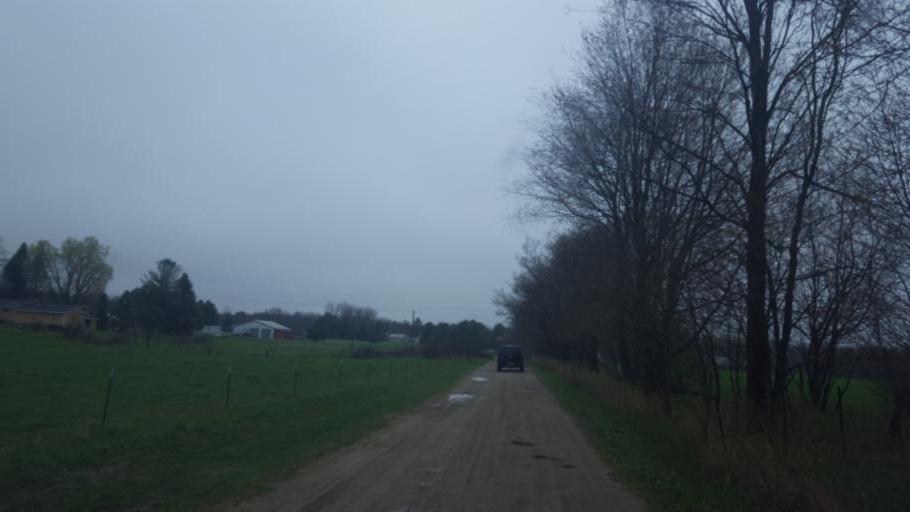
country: US
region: Michigan
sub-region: Isabella County
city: Lake Isabella
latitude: 43.5516
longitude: -84.9715
